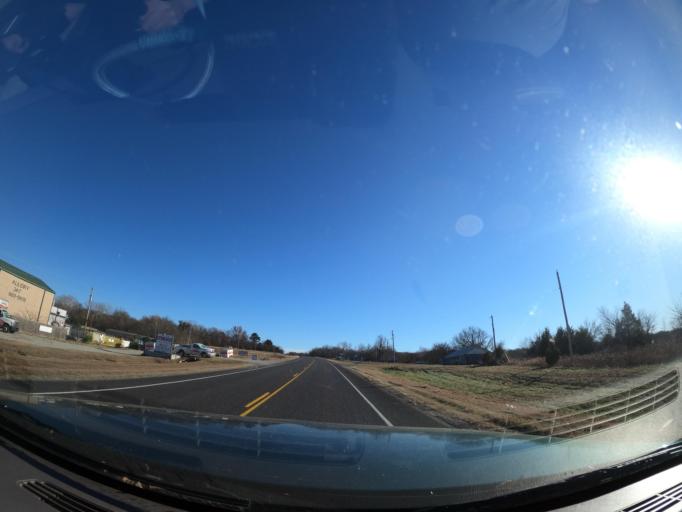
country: US
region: Oklahoma
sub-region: McIntosh County
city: Eufaula
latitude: 35.2556
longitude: -95.5768
